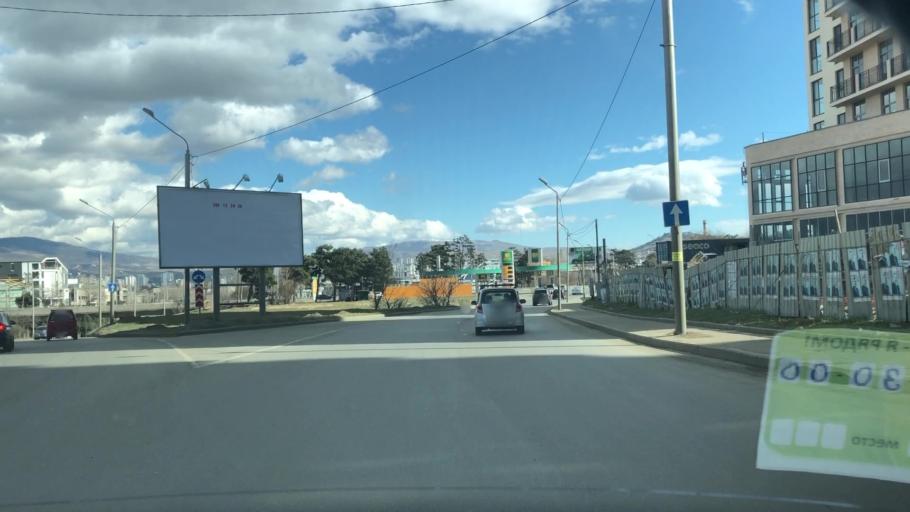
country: GE
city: Zahesi
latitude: 41.7867
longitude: 44.7668
